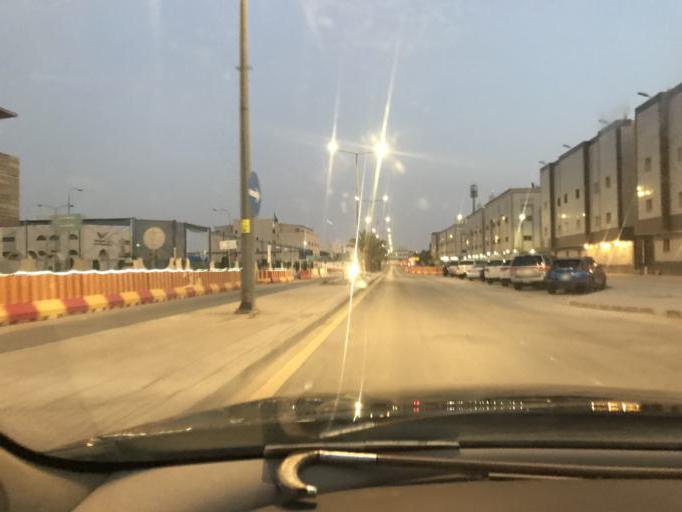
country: SA
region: Ar Riyad
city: Riyadh
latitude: 24.8006
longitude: 46.7078
